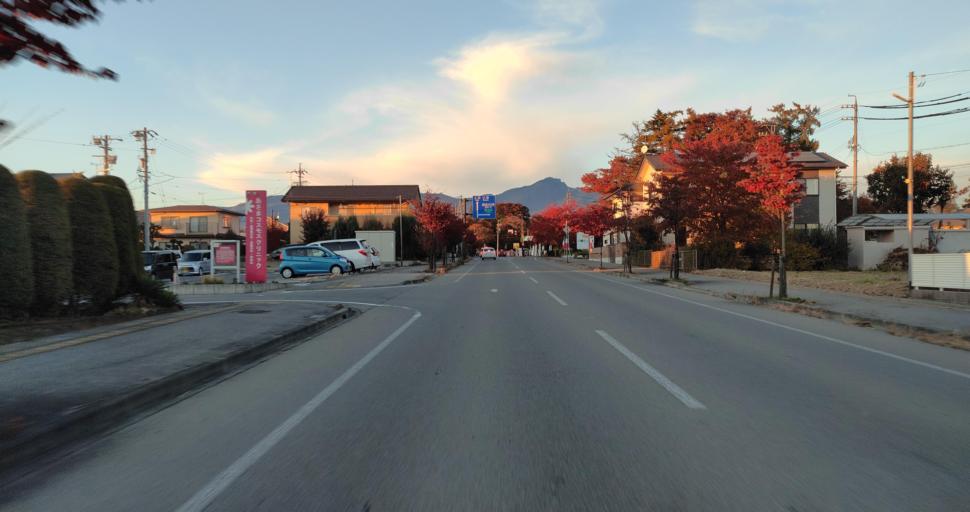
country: JP
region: Nagano
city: Komoro
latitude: 36.2841
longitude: 138.4611
